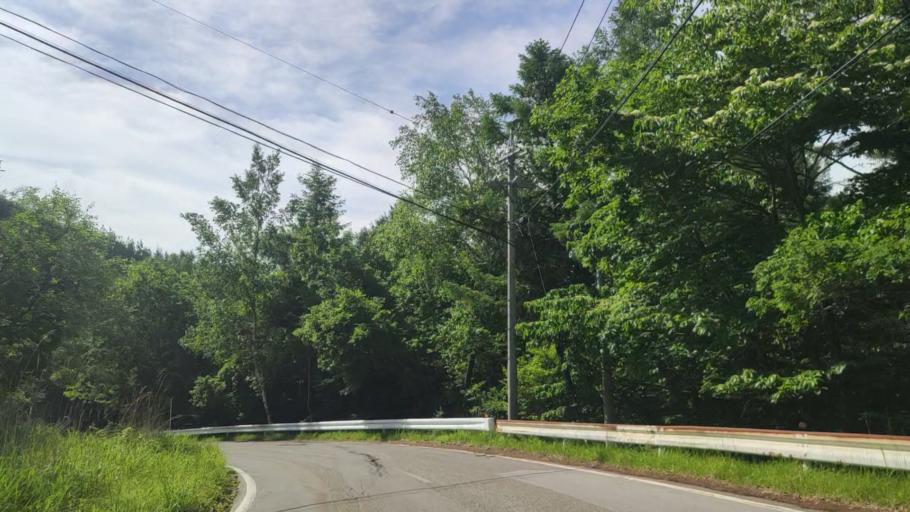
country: JP
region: Nagano
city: Suwa
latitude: 36.0913
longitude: 138.1455
